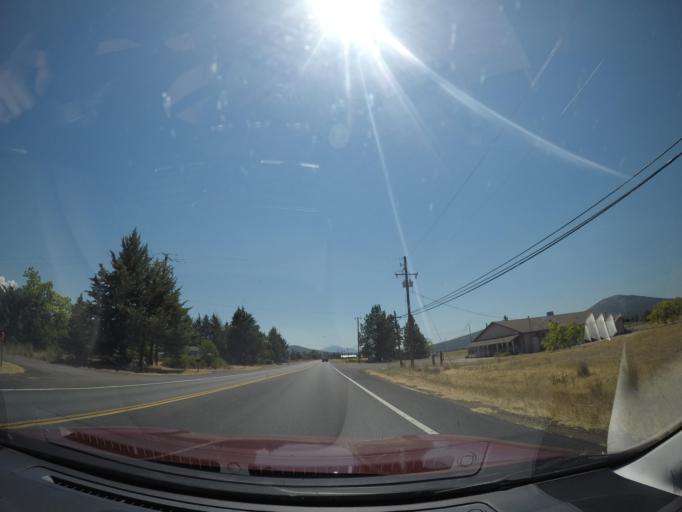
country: US
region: California
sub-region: Shasta County
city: Burney
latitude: 41.0224
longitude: -121.4262
